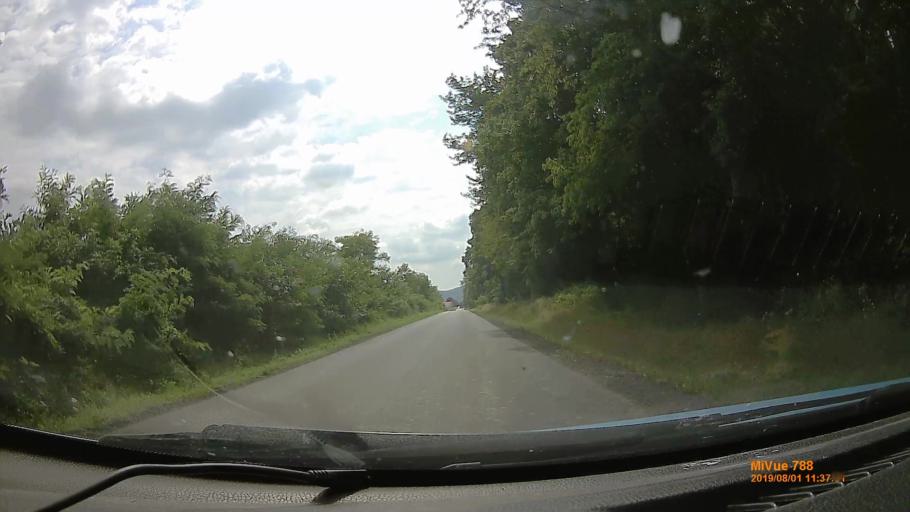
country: HU
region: Baranya
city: Villany
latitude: 45.9059
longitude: 18.3836
